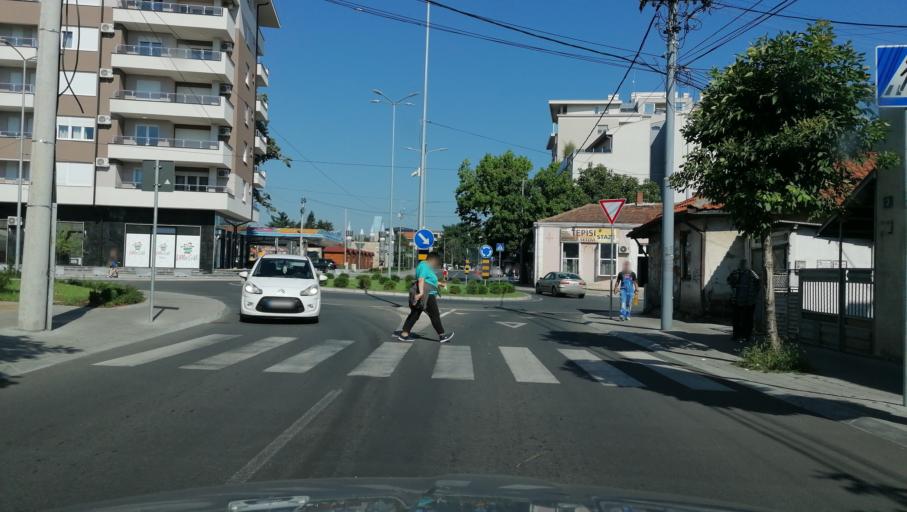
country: RS
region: Central Serbia
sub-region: Rasinski Okrug
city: Krusevac
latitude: 43.5761
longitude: 21.3339
